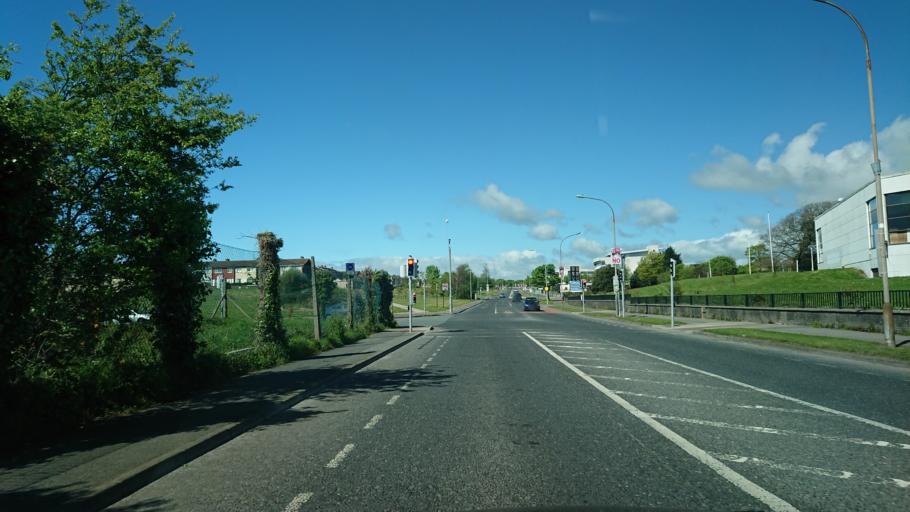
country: IE
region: Munster
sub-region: Waterford
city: Waterford
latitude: 52.2453
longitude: -7.1313
